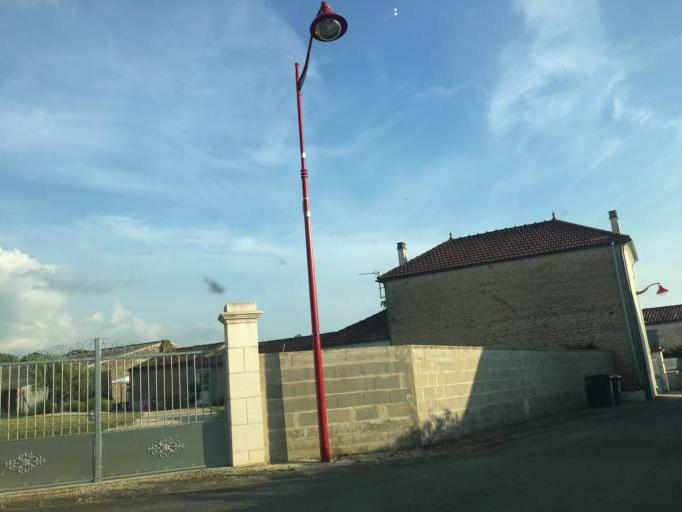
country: FR
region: Poitou-Charentes
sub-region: Departement de la Charente-Maritime
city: Saint-Jean-d'Angely
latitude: 46.0640
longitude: -0.5759
